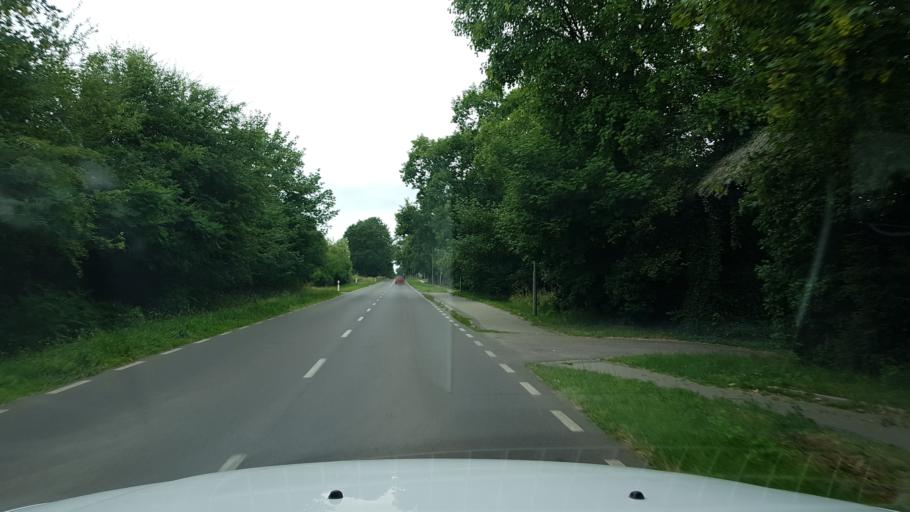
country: PL
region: West Pomeranian Voivodeship
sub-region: Powiat gryficki
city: Brojce
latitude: 53.9582
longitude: 15.3396
